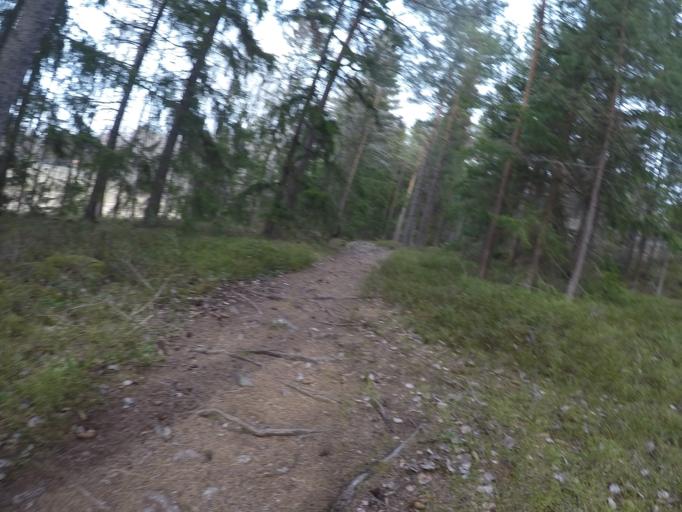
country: SE
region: Soedermanland
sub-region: Eskilstuna Kommun
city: Torshalla
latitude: 59.4324
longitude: 16.5059
